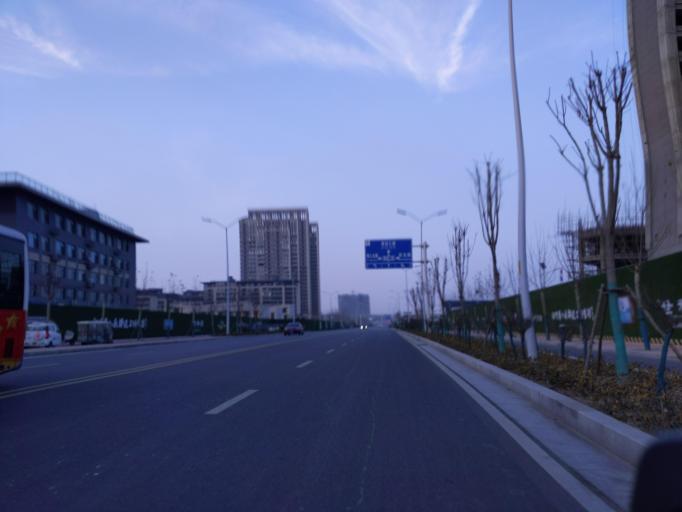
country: CN
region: Henan Sheng
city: Puyang
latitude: 35.8054
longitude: 115.0112
